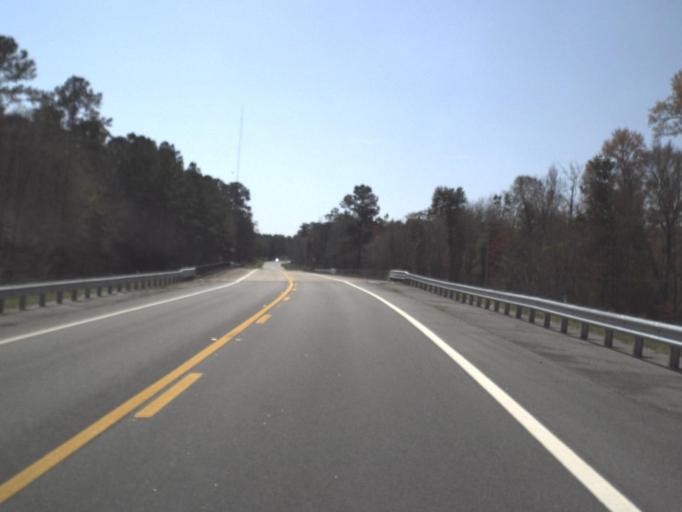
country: US
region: Florida
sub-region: Jefferson County
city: Monticello
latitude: 30.4756
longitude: -84.0224
